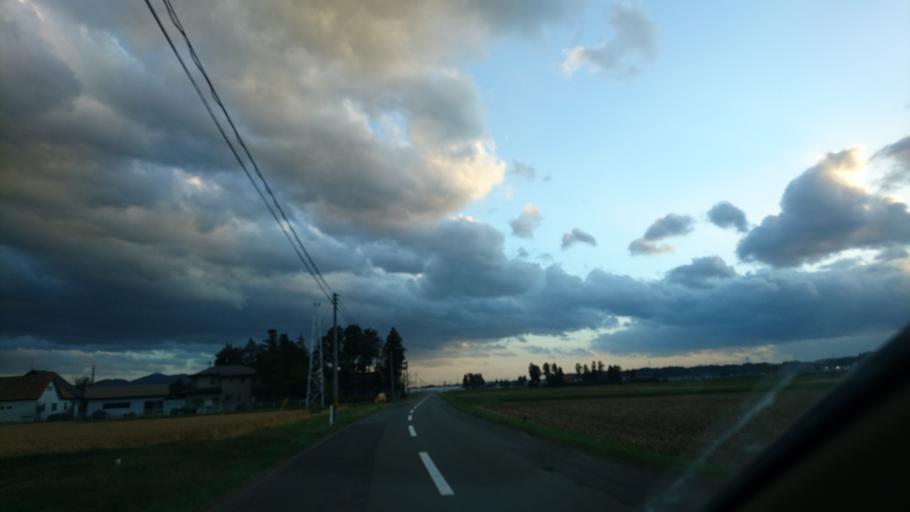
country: JP
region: Iwate
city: Mizusawa
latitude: 39.1101
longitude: 141.1503
